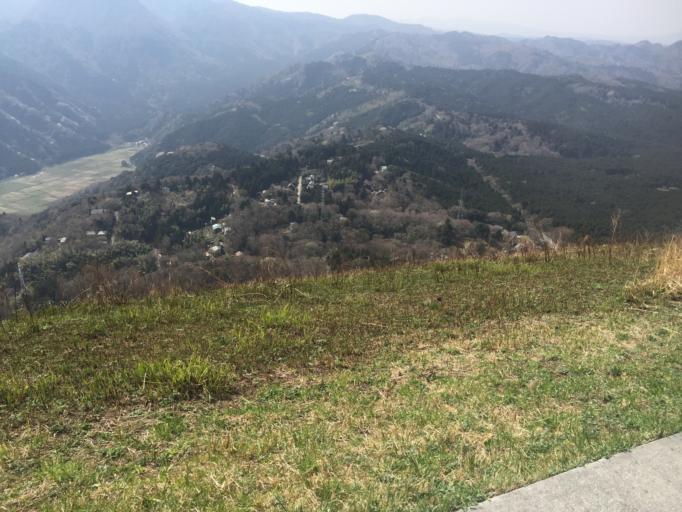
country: JP
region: Shizuoka
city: Ito
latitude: 34.9034
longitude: 139.0942
